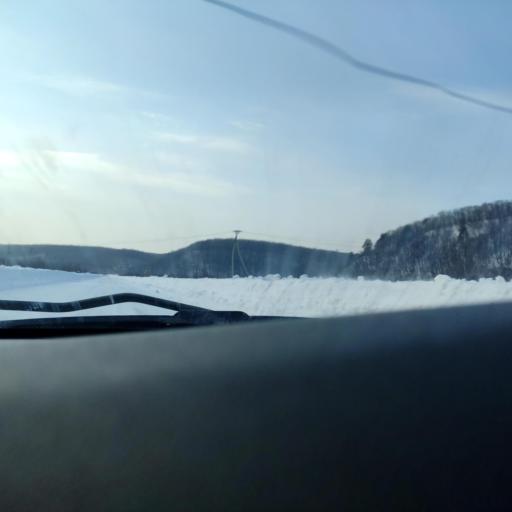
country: RU
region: Samara
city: Novokuybyshevsk
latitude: 53.2424
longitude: 49.8404
